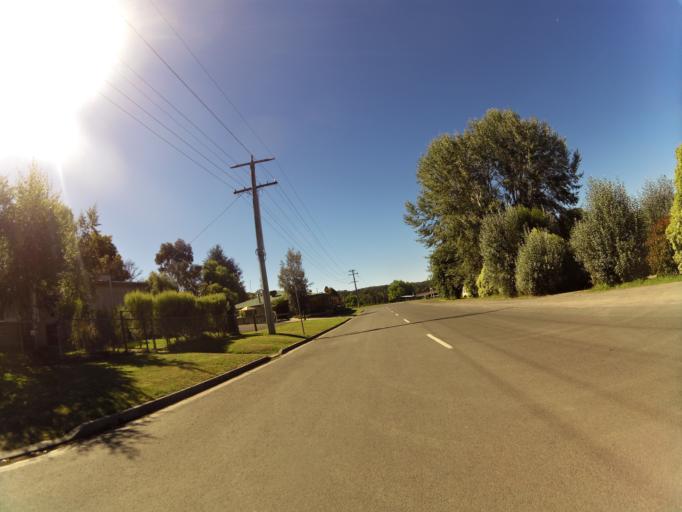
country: AU
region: Victoria
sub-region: Colac-Otway
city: Colac
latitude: -38.5163
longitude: 143.7165
